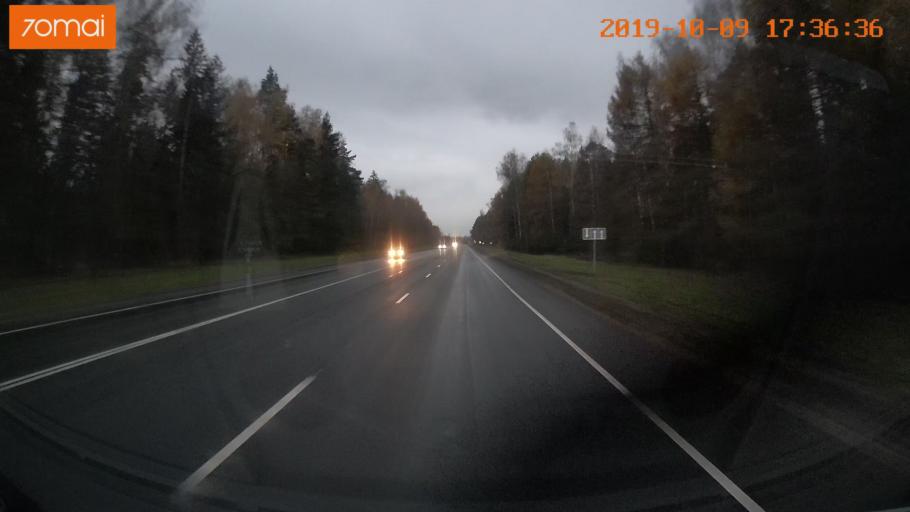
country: RU
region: Ivanovo
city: Bogorodskoye
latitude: 57.0762
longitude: 40.9951
